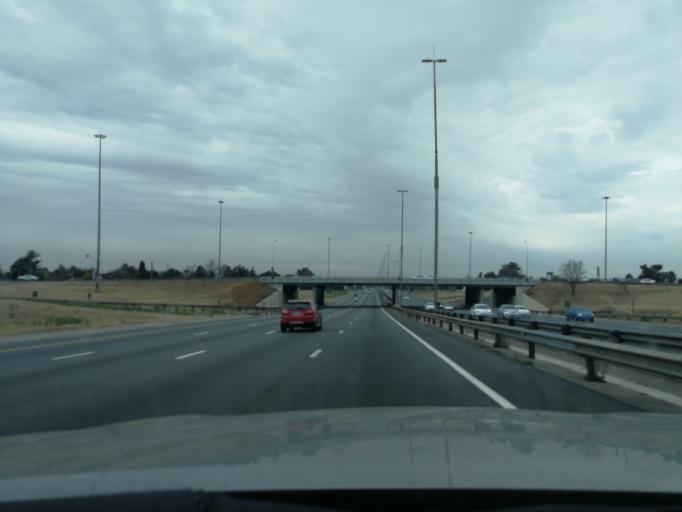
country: ZA
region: Gauteng
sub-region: Ekurhuleni Metropolitan Municipality
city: Germiston
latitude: -26.2643
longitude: 28.1507
